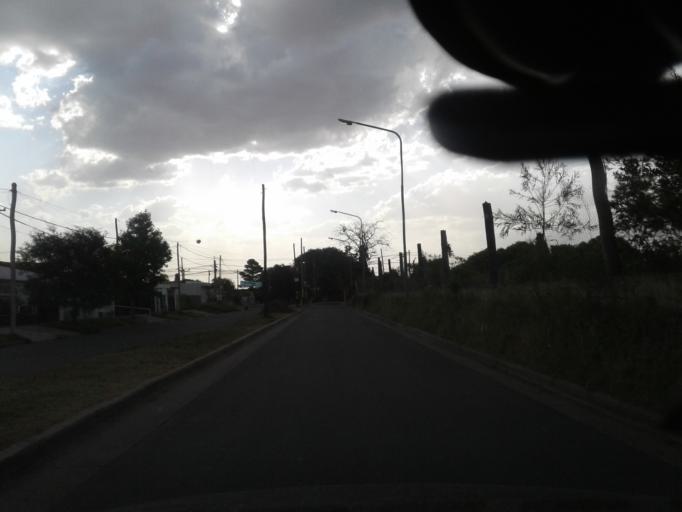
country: AR
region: Santa Fe
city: Granadero Baigorria
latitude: -32.8835
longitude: -60.7271
